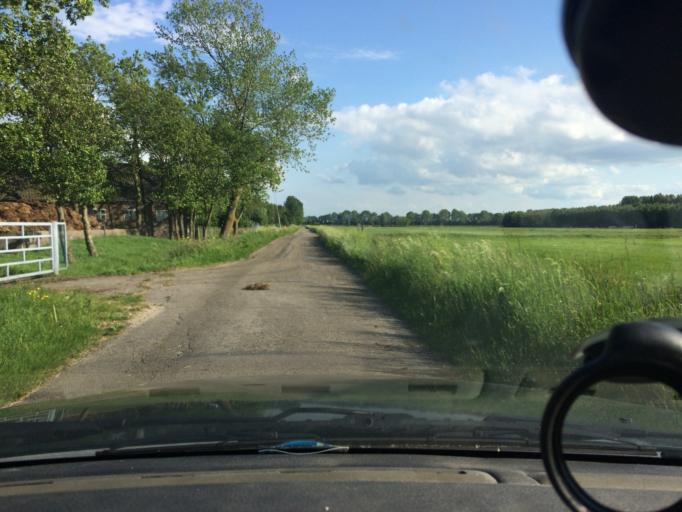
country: NL
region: North Holland
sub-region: Gemeente Haarlem
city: Haarlem
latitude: 52.3932
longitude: 4.7110
